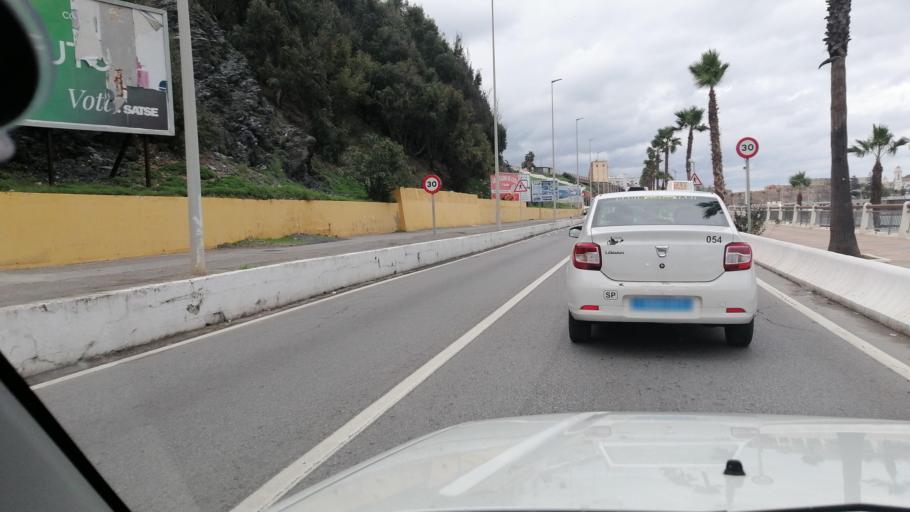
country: ES
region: Ceuta
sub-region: Ceuta
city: Ceuta
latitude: 35.8837
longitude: -5.3240
